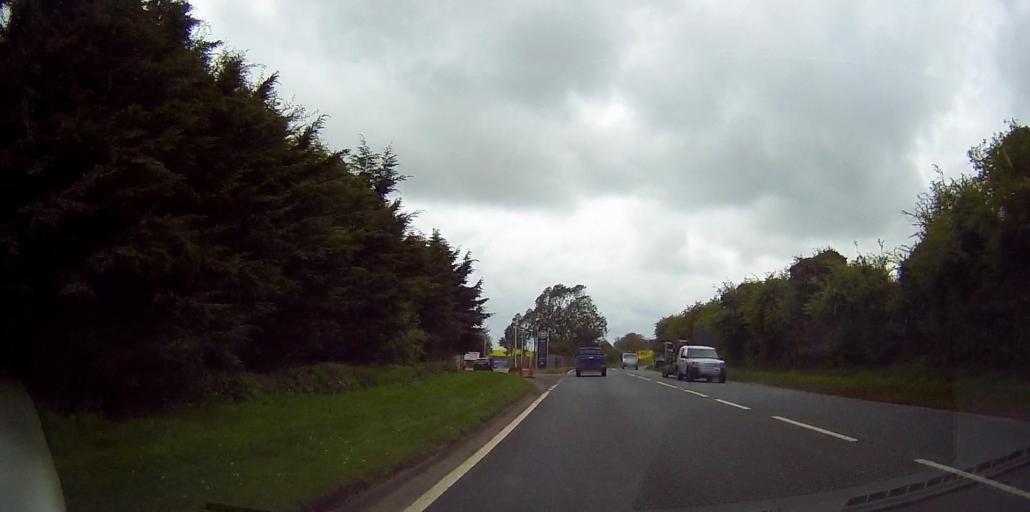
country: GB
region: England
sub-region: Kent
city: Lenham
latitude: 51.2139
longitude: 0.7875
